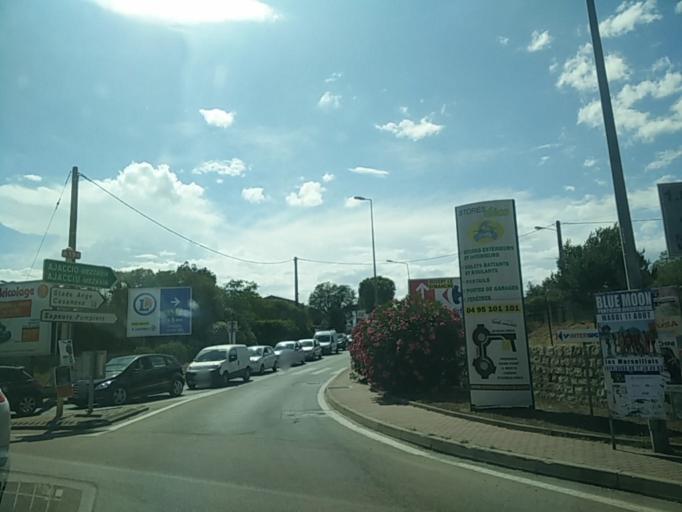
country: FR
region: Corsica
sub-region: Departement de la Corse-du-Sud
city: Afa
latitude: 41.9526
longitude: 8.7828
